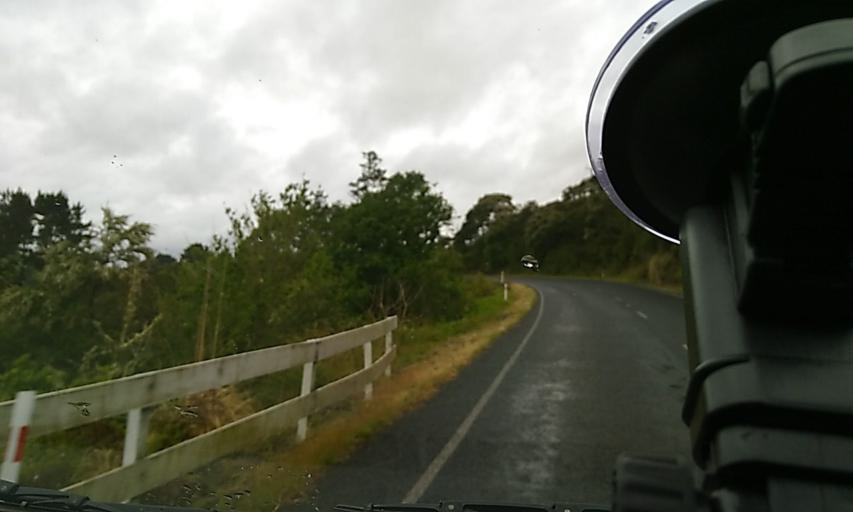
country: NZ
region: Auckland
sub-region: Auckland
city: Pukekohe East
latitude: -37.3210
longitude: 174.9289
